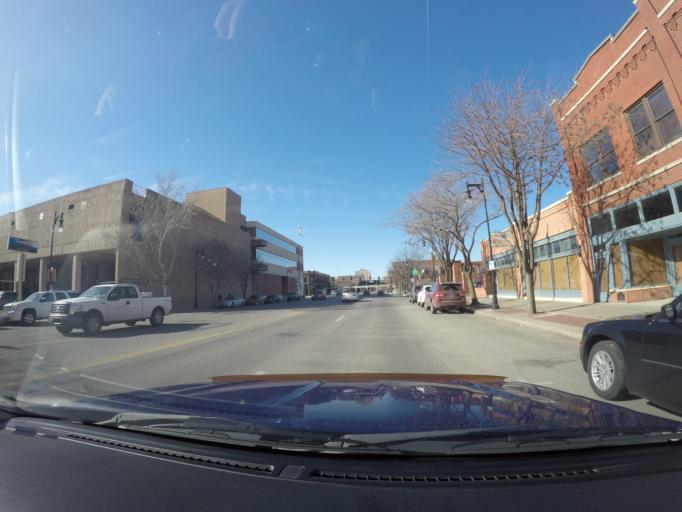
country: US
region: Kansas
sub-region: Sedgwick County
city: Wichita
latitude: 37.6861
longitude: -97.3271
